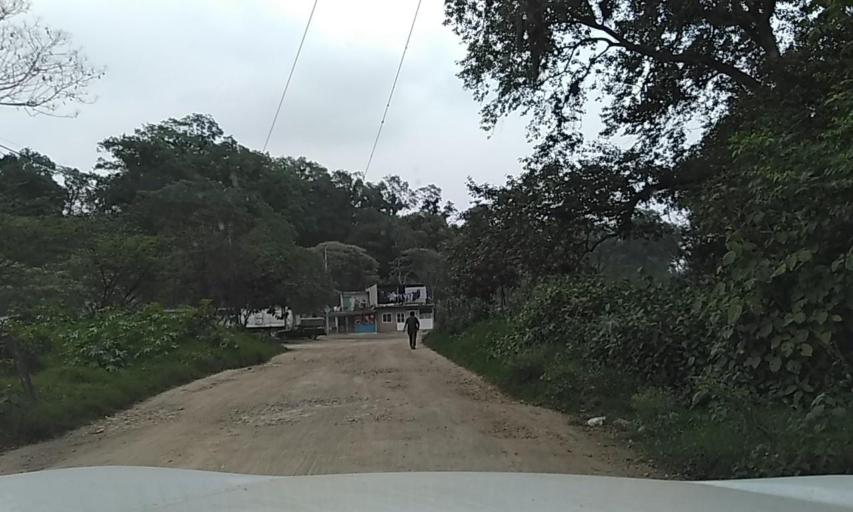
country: MX
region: Veracruz
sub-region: Jilotepec
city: El Pueblito (Garbanzal)
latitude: 19.5724
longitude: -96.8947
